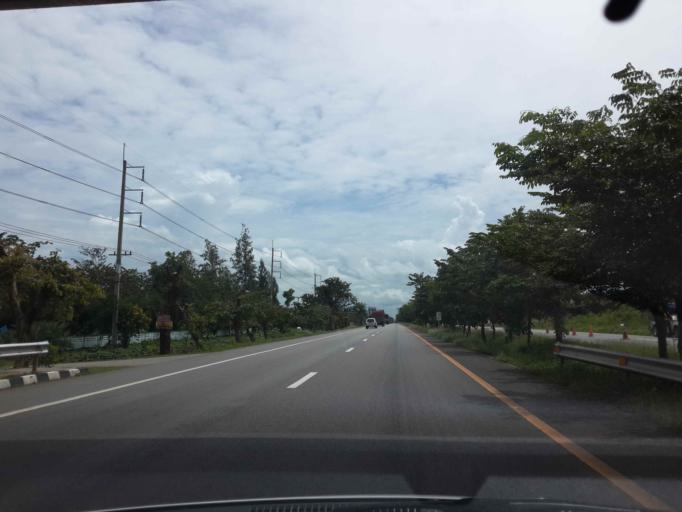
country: TH
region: Ratchaburi
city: Pak Tho
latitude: 13.4123
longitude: 99.8113
